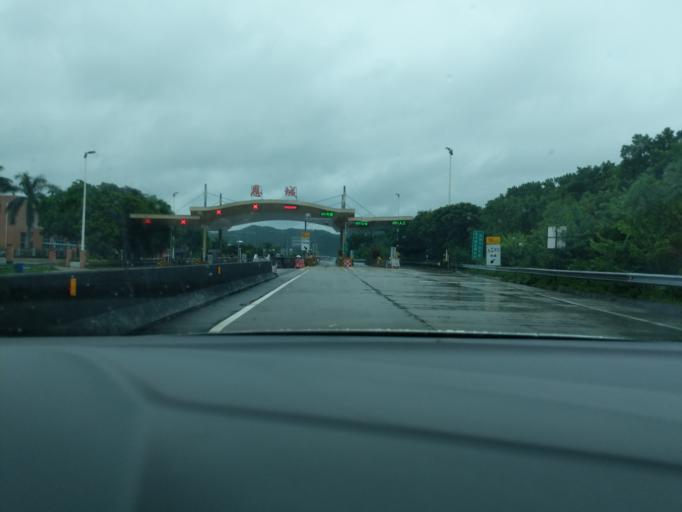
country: CN
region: Guangdong
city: Pingshi
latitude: 22.2379
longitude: 112.3063
